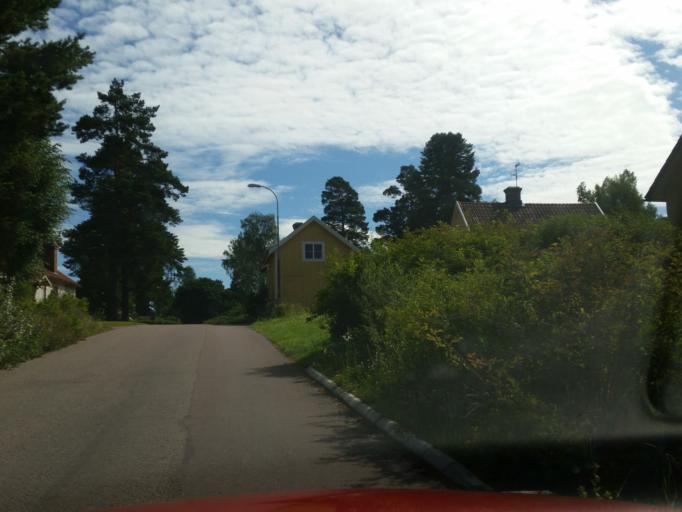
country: SE
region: Dalarna
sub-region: Leksand Municipality
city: Smedby
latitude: 60.6721
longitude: 15.0897
